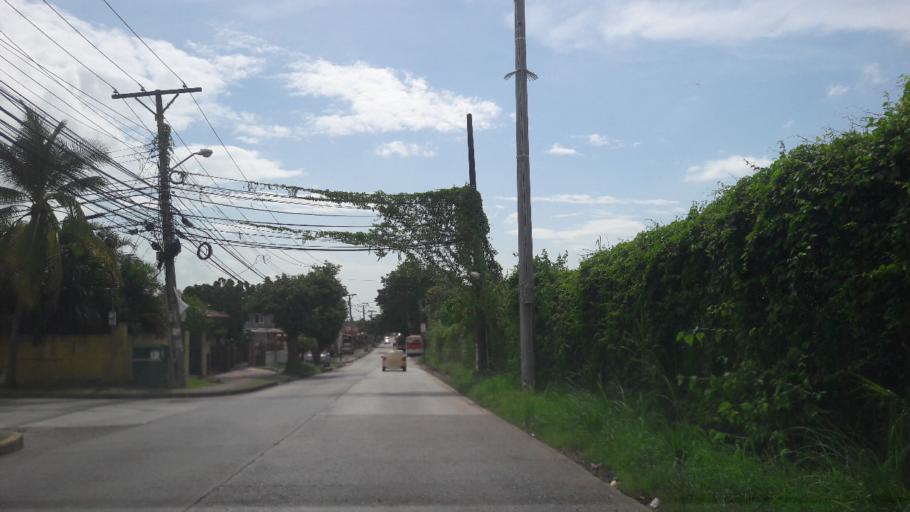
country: PA
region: Panama
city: Tocumen
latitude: 9.0612
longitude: -79.4208
